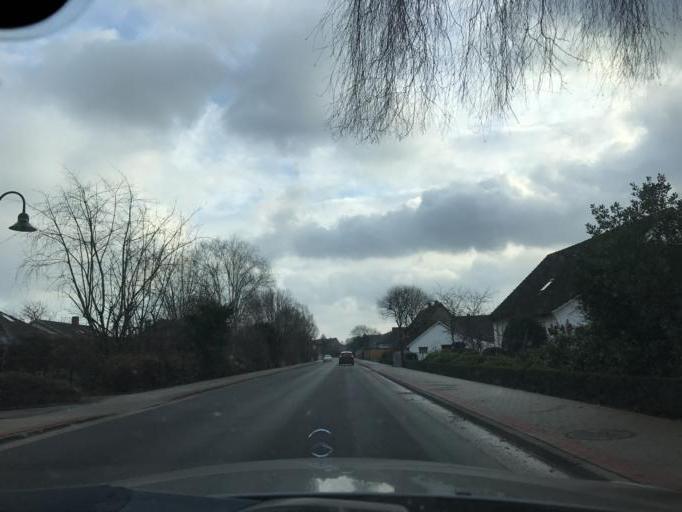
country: DE
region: Lower Saxony
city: Hasbergen
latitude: 52.2031
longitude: 7.9312
